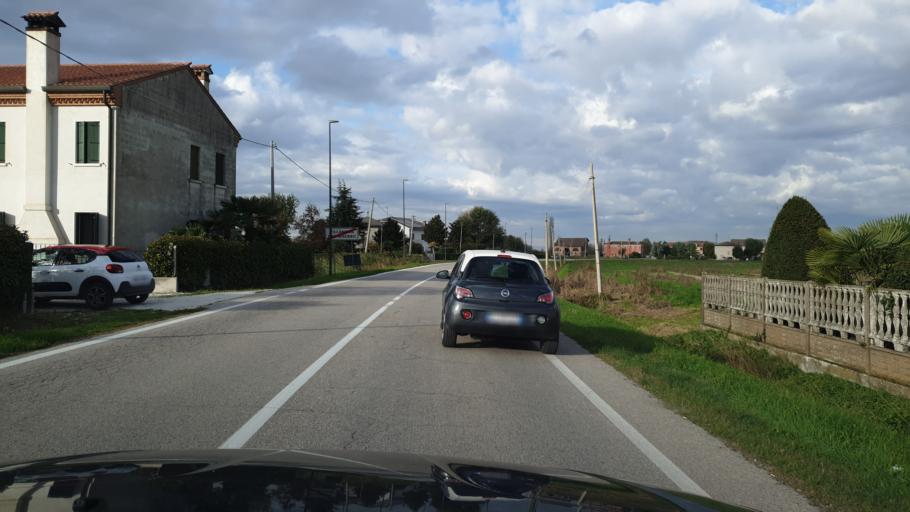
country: IT
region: Veneto
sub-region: Provincia di Rovigo
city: Villanova del Ghebbo Canton
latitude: 45.0622
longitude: 11.6300
